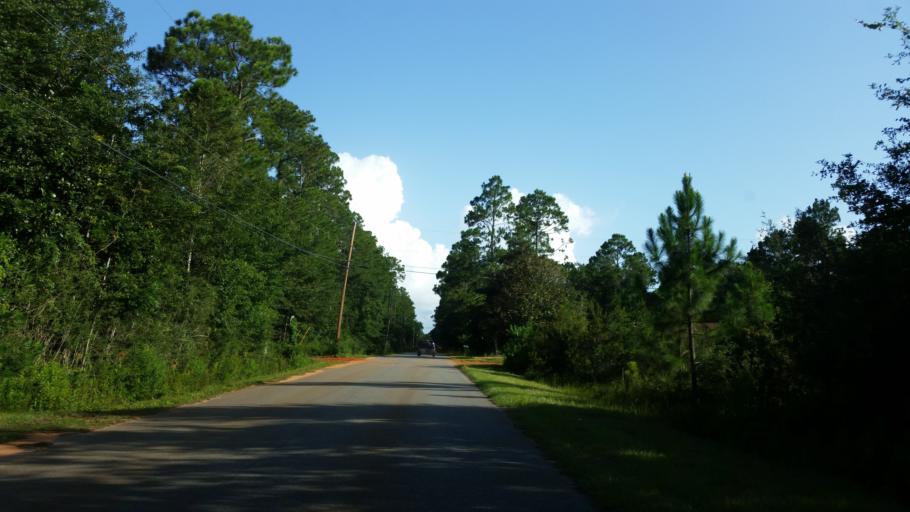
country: US
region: Florida
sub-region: Santa Rosa County
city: Pace
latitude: 30.5430
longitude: -87.1062
